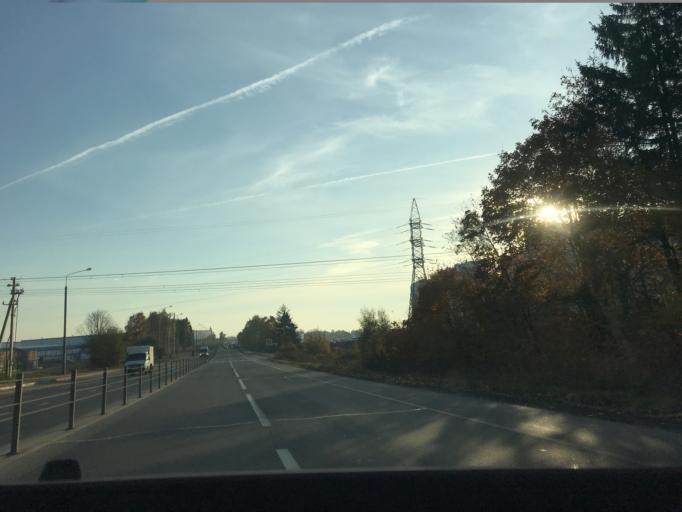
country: RU
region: Moskovskaya
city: Yam
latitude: 55.4751
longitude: 37.7136
